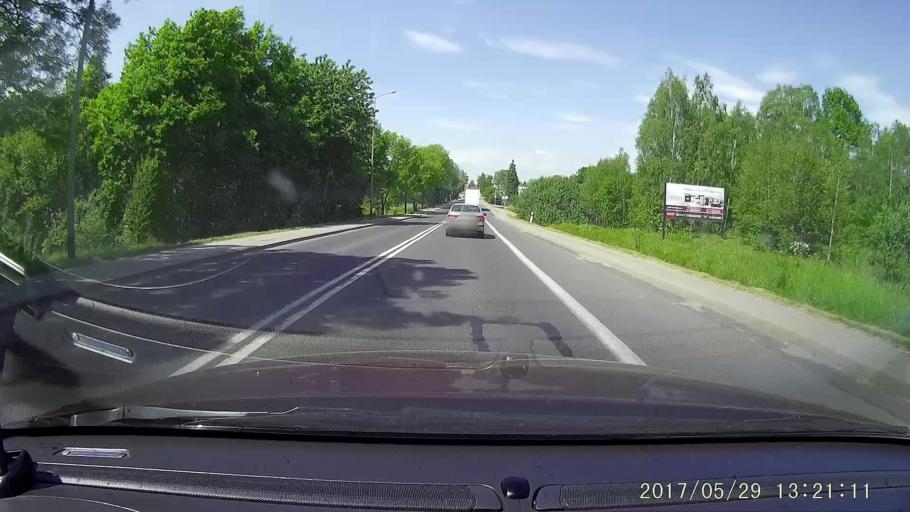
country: PL
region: Lower Silesian Voivodeship
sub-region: Powiat lwowecki
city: Gryfow Slaski
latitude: 51.0281
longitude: 15.4229
